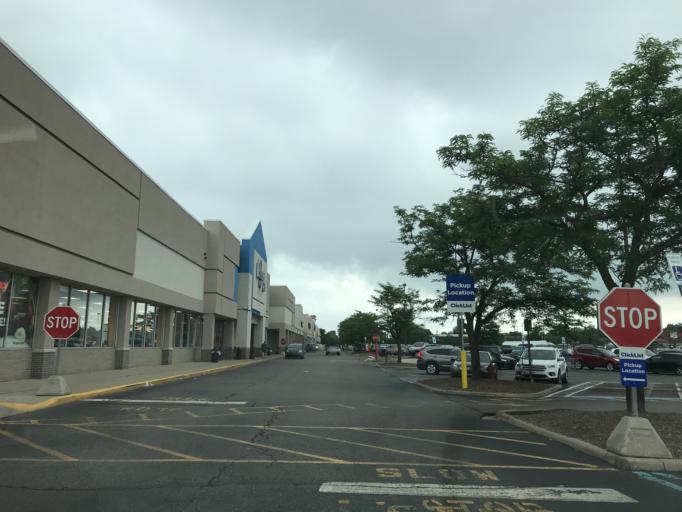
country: US
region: Michigan
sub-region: Washtenaw County
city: Ypsilanti
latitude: 42.2423
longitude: -83.6817
